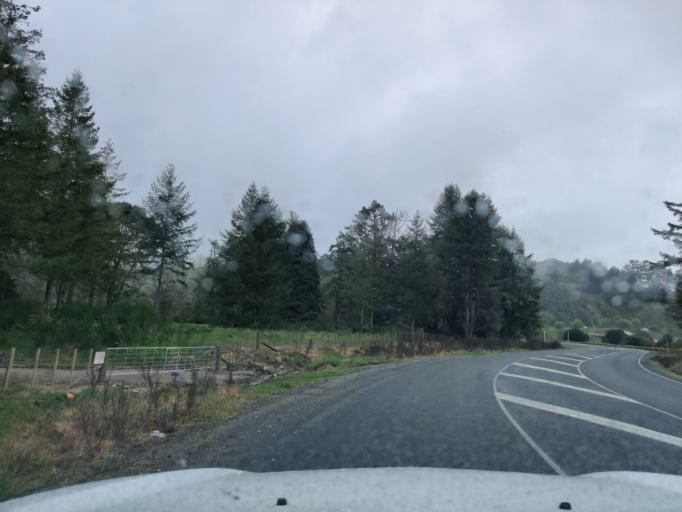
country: NZ
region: Bay of Plenty
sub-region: Rotorua District
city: Rotorua
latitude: -38.1774
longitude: 176.2508
